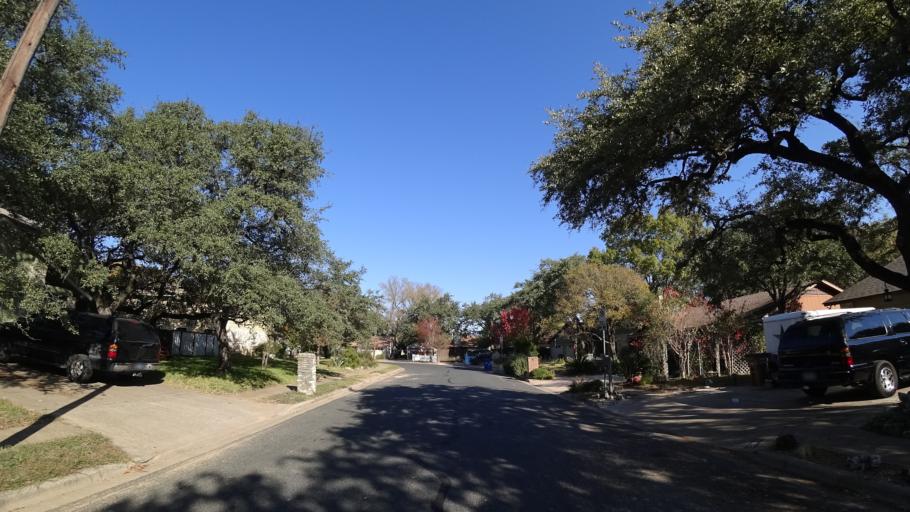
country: US
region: Texas
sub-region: Travis County
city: Barton Creek
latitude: 30.2284
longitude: -97.8418
